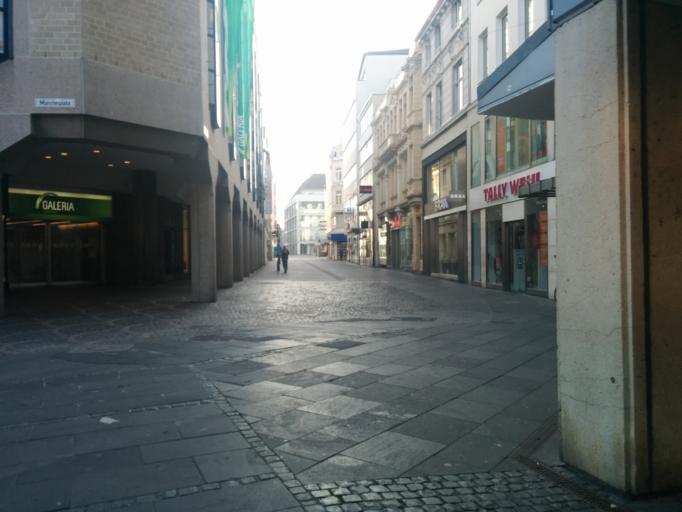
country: DE
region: North Rhine-Westphalia
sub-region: Regierungsbezirk Koln
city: Bonn
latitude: 50.7339
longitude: 7.1001
